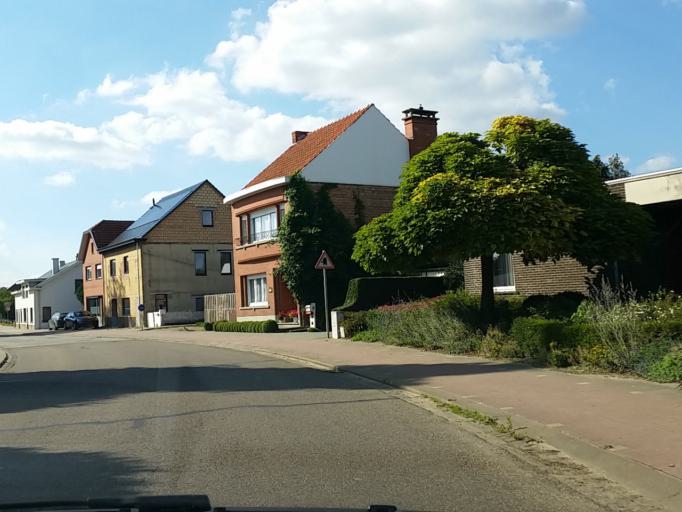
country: BE
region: Flanders
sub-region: Provincie Vlaams-Brabant
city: Holsbeek
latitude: 50.9258
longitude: 4.8011
